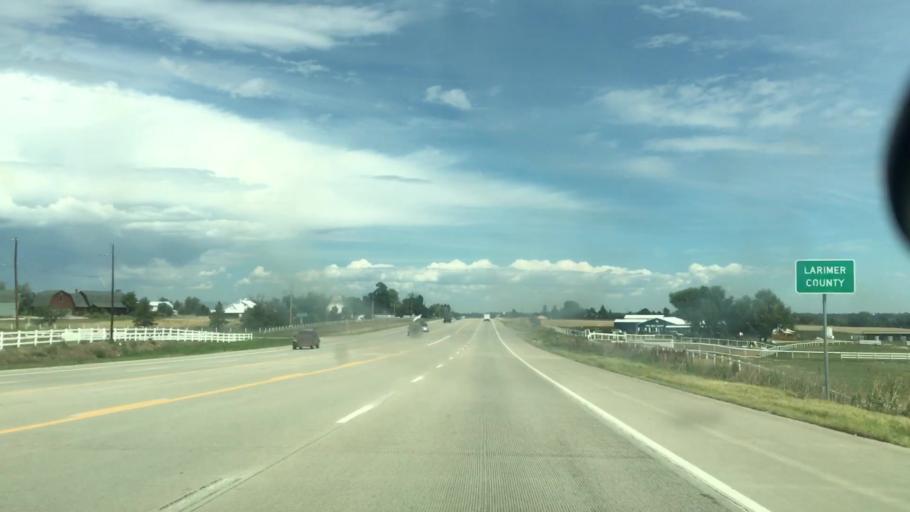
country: US
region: Colorado
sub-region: Larimer County
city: Berthoud
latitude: 40.2616
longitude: -105.1024
